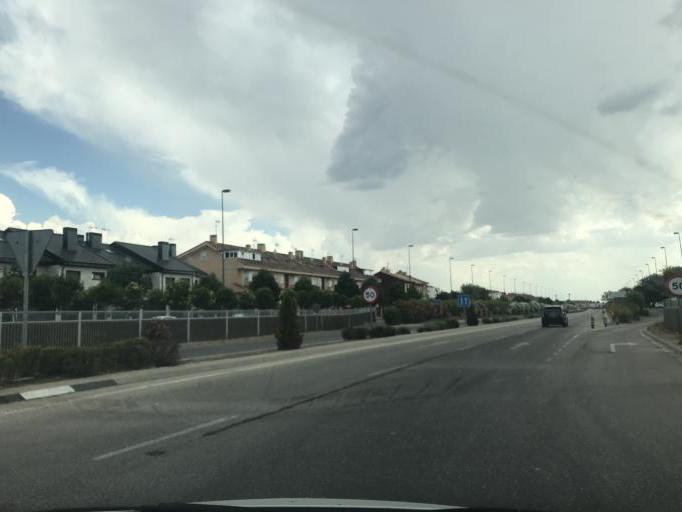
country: ES
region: Madrid
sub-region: Provincia de Madrid
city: Paracuellos de Jarama
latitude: 40.5103
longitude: -3.5142
